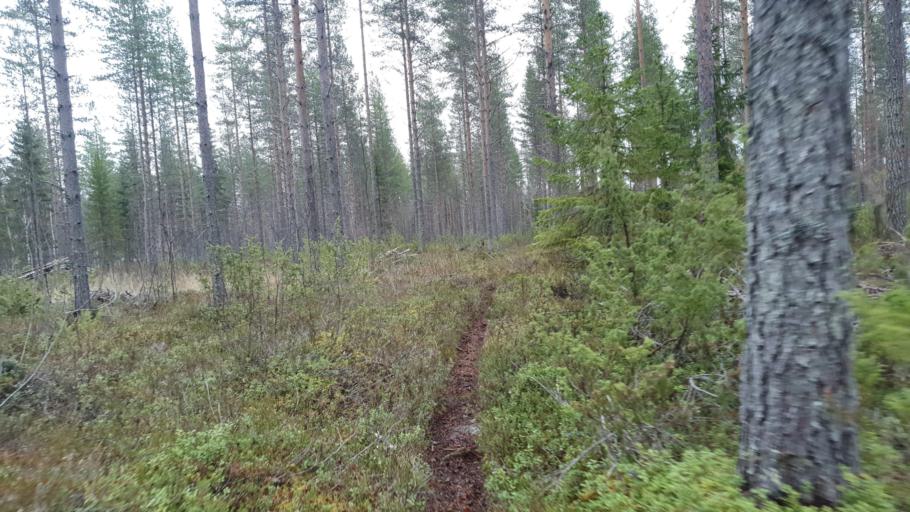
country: FI
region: Kainuu
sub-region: Kehys-Kainuu
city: Kuhmo
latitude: 64.1346
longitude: 29.4026
